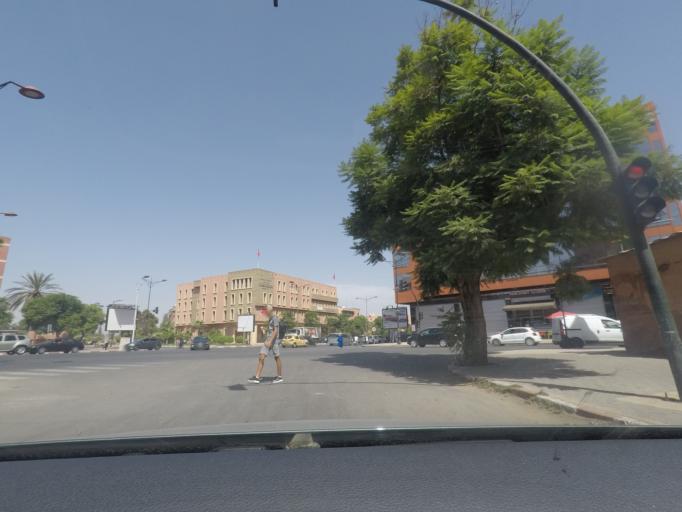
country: MA
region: Marrakech-Tensift-Al Haouz
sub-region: Marrakech
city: Marrakesh
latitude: 31.6322
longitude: -8.0161
